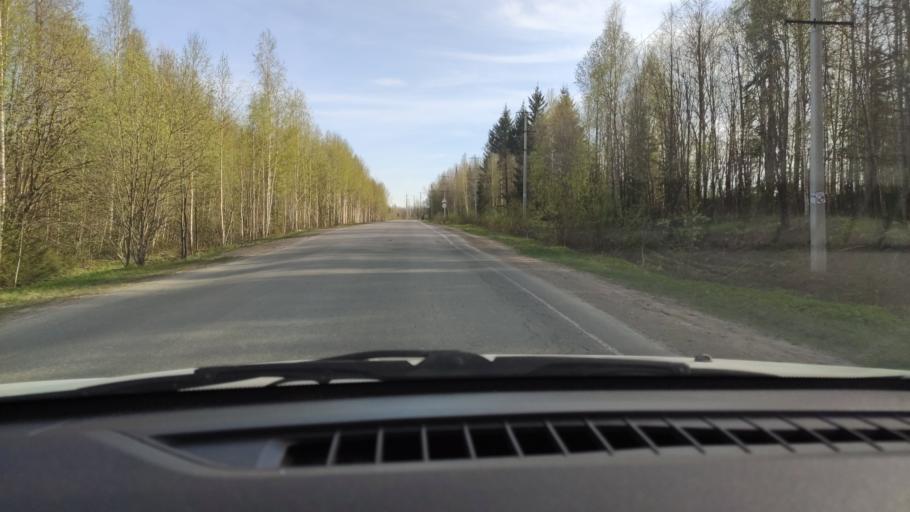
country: RU
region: Perm
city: Novyye Lyady
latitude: 57.9471
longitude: 56.5687
